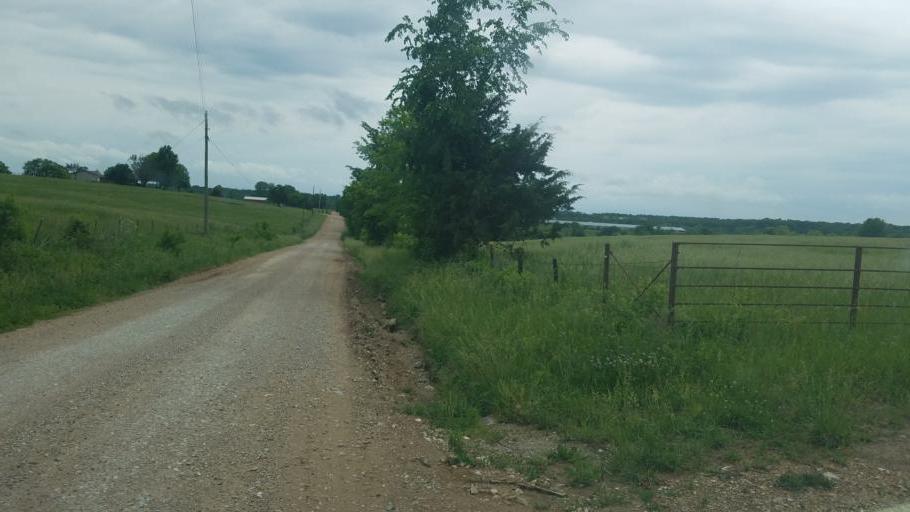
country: US
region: Missouri
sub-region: Moniteau County
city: California
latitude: 38.6181
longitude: -92.6194
